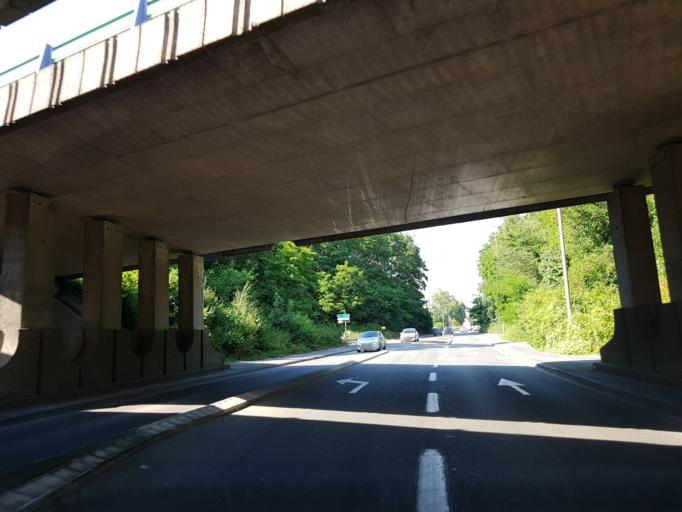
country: FR
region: Nord-Pas-de-Calais
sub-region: Departement du Nord
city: Escaudain
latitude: 50.3247
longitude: 3.3429
